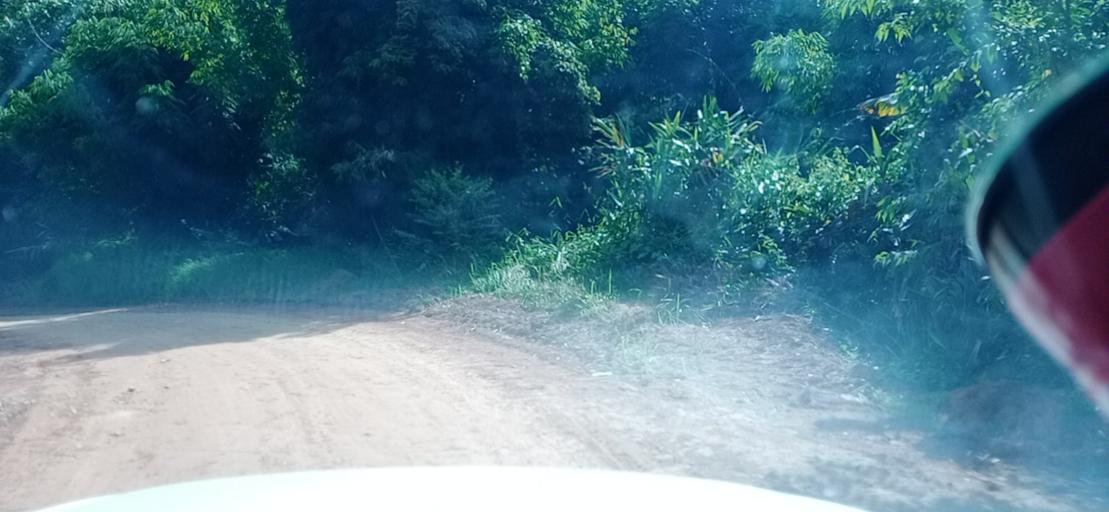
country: TH
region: Changwat Bueng Kan
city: Pak Khat
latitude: 18.6372
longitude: 103.2557
